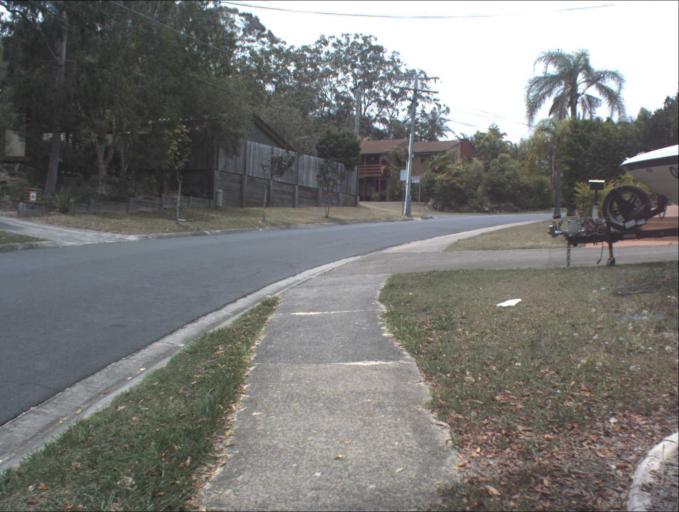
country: AU
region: Queensland
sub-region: Logan
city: Springwood
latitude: -27.6230
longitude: 153.1389
